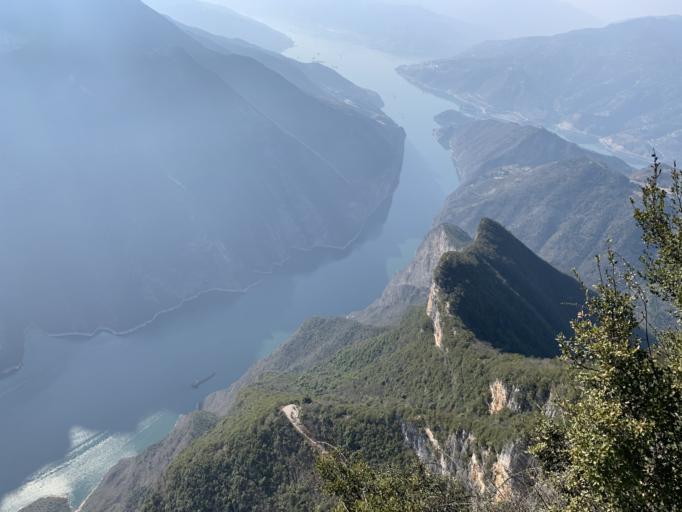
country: CN
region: Chongqing Shi
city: Daxi
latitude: 31.0290
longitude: 109.6201
